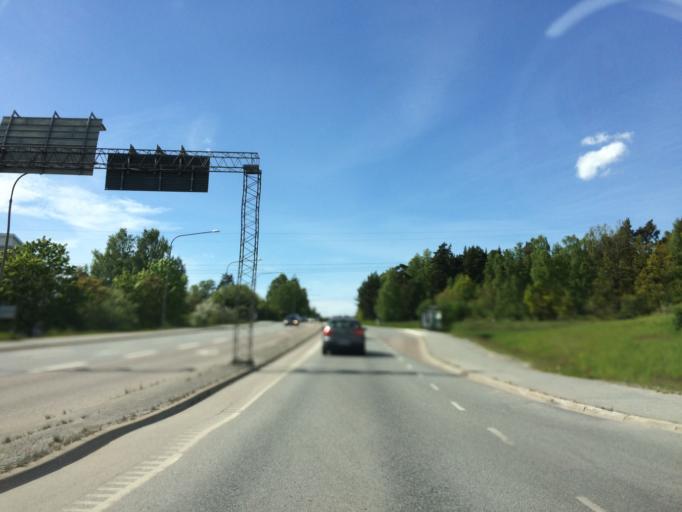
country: SE
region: Stockholm
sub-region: Danderyds Kommun
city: Djursholm
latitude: 59.4106
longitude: 18.0313
